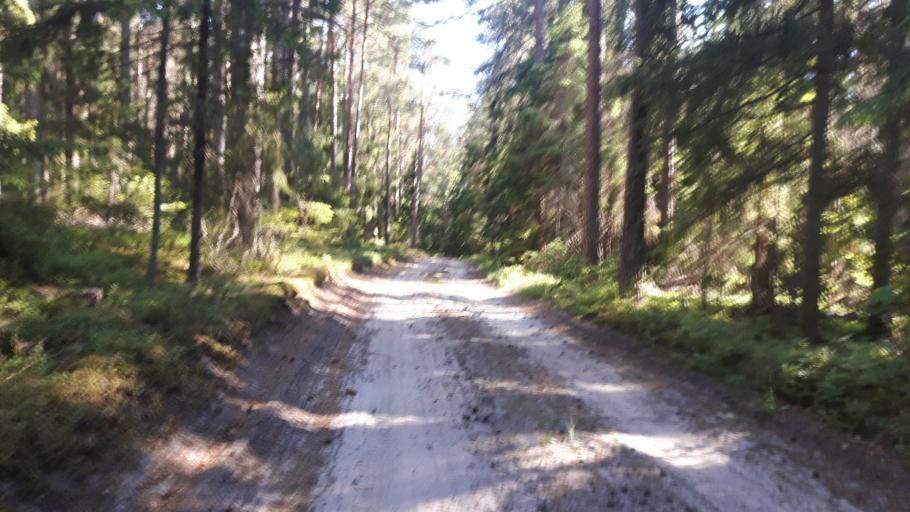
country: LV
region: Salacgrivas
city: Salacgriva
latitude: 57.7217
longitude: 24.3479
